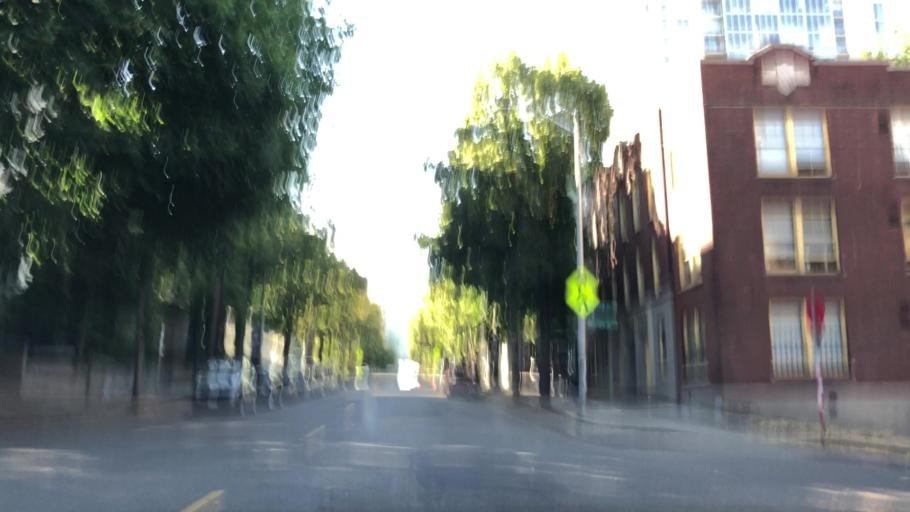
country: US
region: Washington
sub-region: King County
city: Seattle
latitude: 47.6079
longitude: -122.3269
